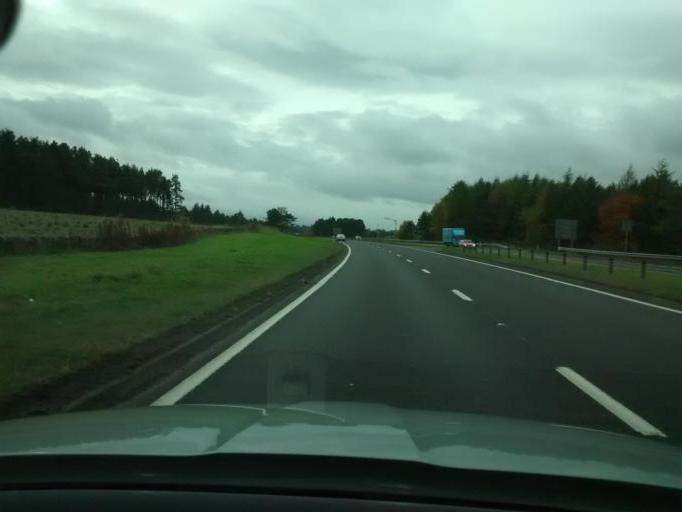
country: GB
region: Scotland
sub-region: Perth and Kinross
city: Perth
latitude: 56.3849
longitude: -3.5043
